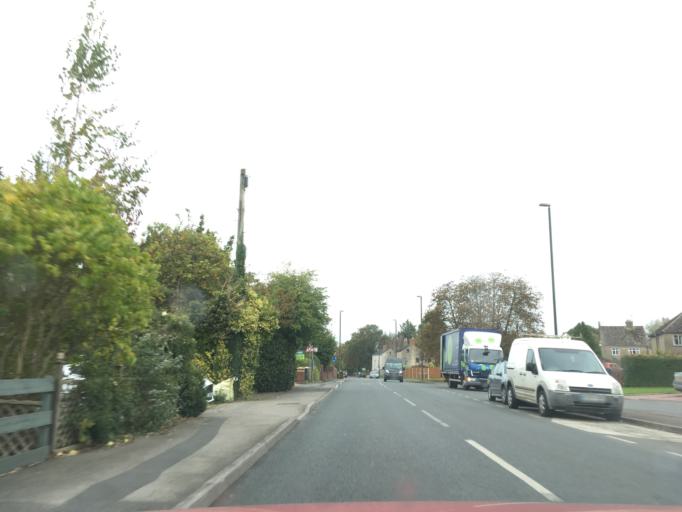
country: GB
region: England
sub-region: Gloucestershire
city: Stonehouse
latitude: 51.7539
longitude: -2.2826
